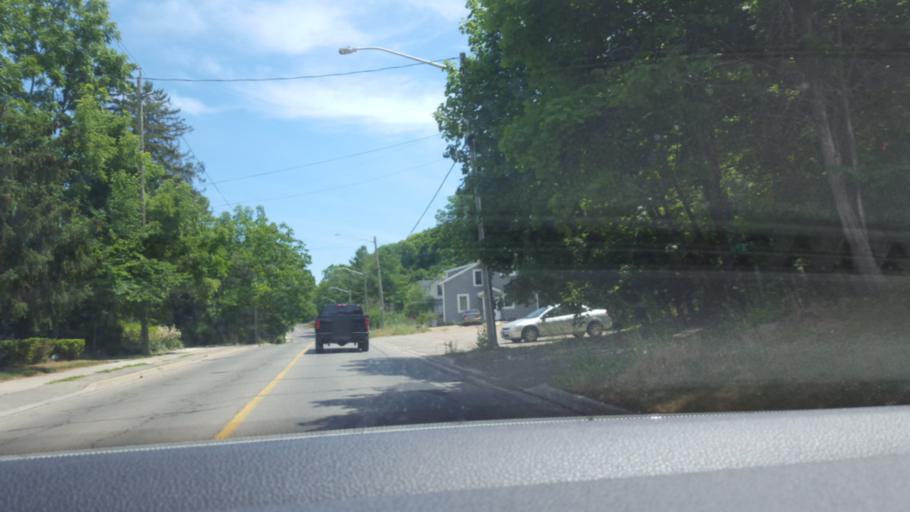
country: CA
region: Ontario
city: Oakville
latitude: 43.1932
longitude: -79.5750
